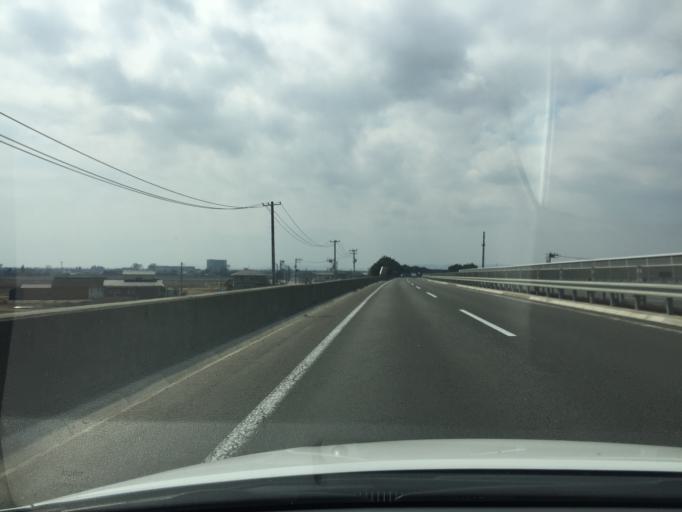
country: JP
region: Miyagi
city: Iwanuma
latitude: 38.1765
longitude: 140.9266
